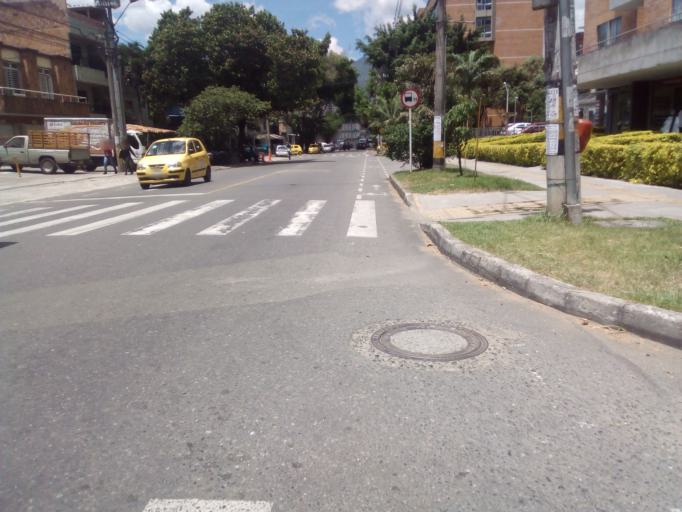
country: CO
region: Antioquia
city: Medellin
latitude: 6.2616
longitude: -75.5867
